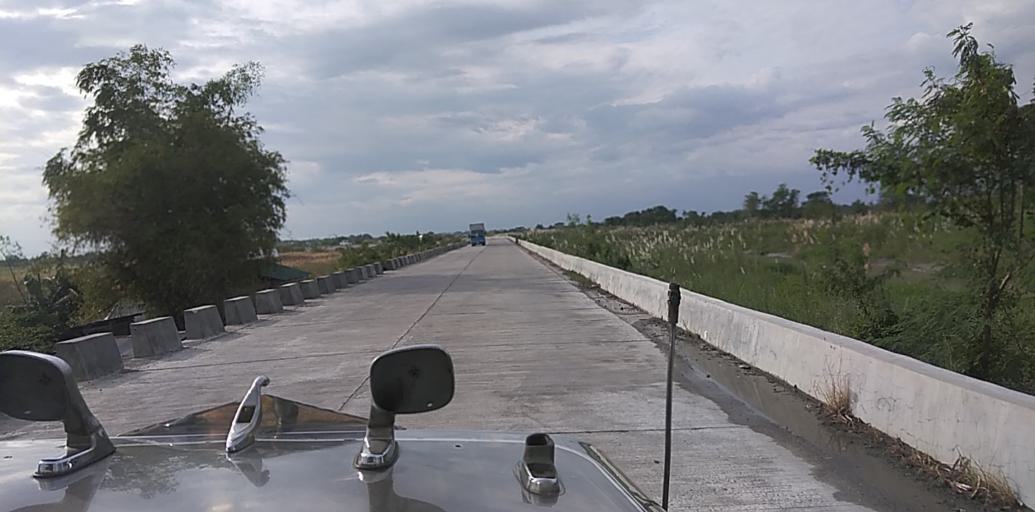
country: PH
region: Central Luzon
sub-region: Province of Pampanga
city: Minalin
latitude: 14.9670
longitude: 120.6673
